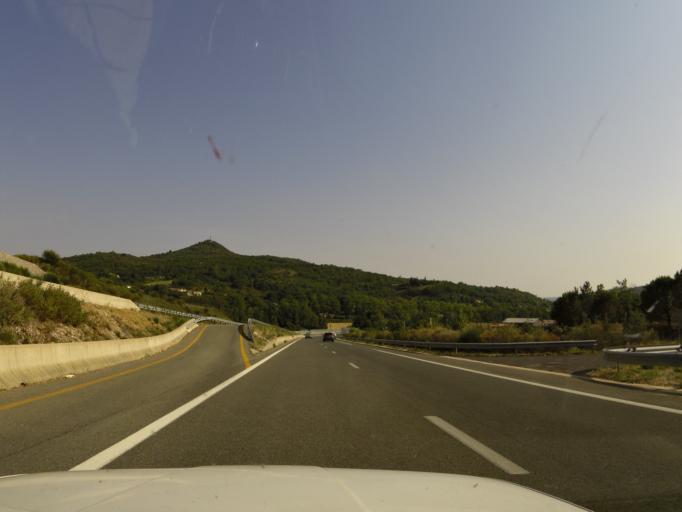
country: FR
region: Languedoc-Roussillon
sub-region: Departement de l'Herault
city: Lodeve
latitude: 43.7697
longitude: 3.3361
